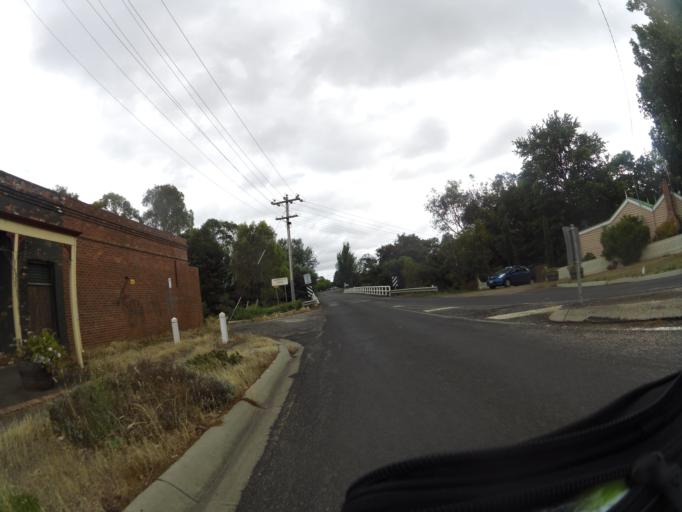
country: AU
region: Victoria
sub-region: Mount Alexander
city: Castlemaine
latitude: -37.0701
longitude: 144.2119
